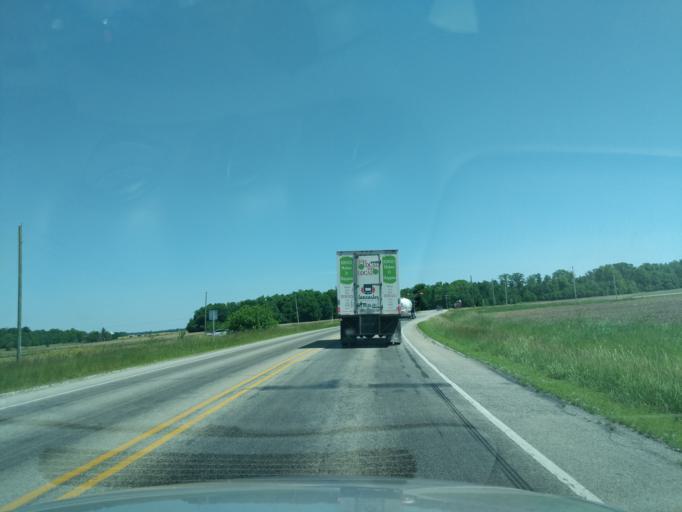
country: US
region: Indiana
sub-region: Huntington County
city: Roanoke
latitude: 41.0032
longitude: -85.4717
